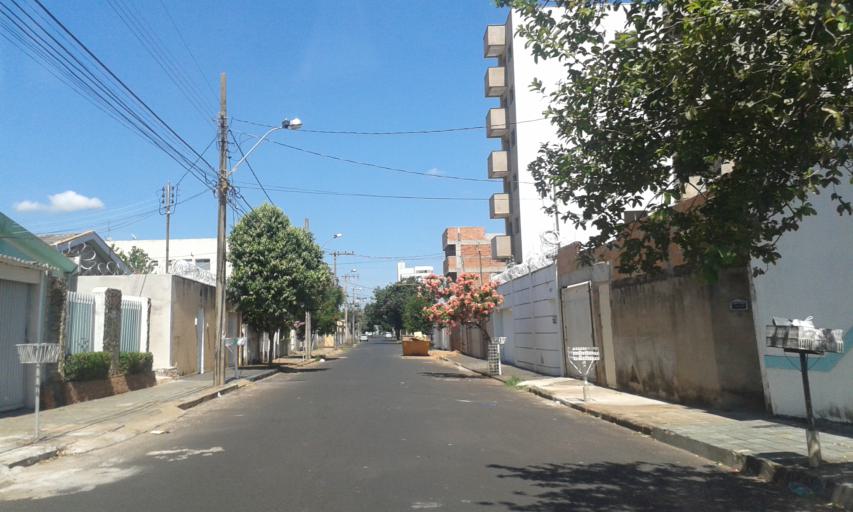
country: BR
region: Minas Gerais
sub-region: Uberlandia
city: Uberlandia
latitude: -18.9225
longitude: -48.2644
